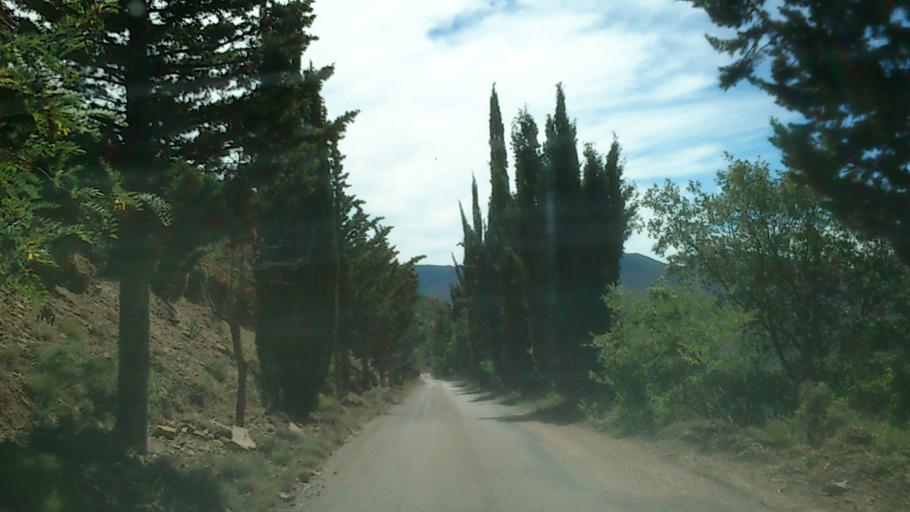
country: ES
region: Aragon
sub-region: Provincia de Huesca
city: Arguis
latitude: 42.3279
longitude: -0.4035
